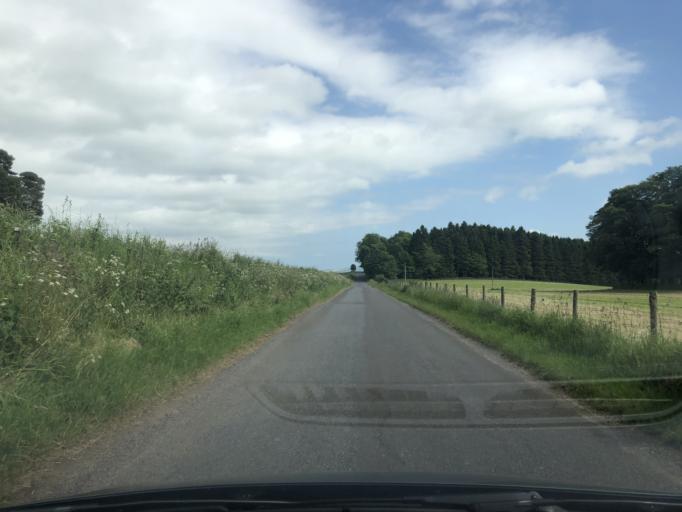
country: GB
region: Scotland
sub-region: Angus
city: Kirriemuir
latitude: 56.7247
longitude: -2.9726
